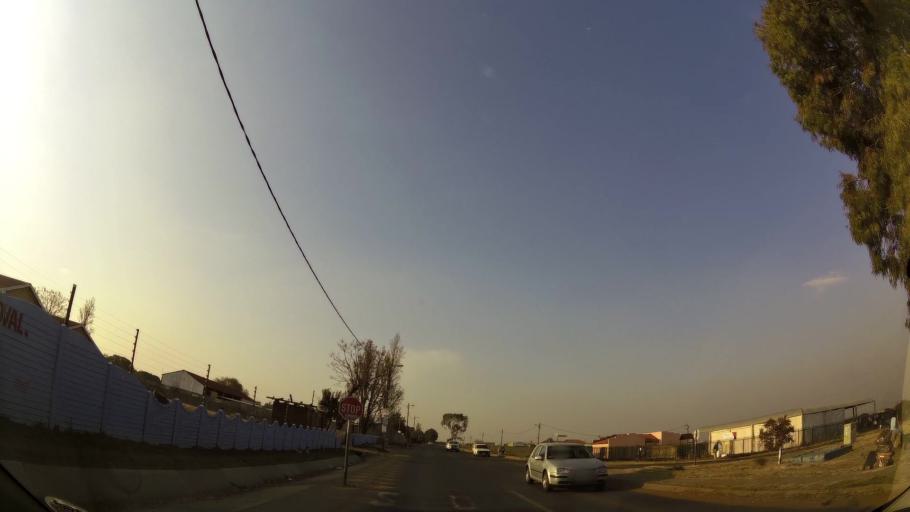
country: ZA
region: Gauteng
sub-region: Ekurhuleni Metropolitan Municipality
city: Benoni
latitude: -26.1549
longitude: 28.3781
